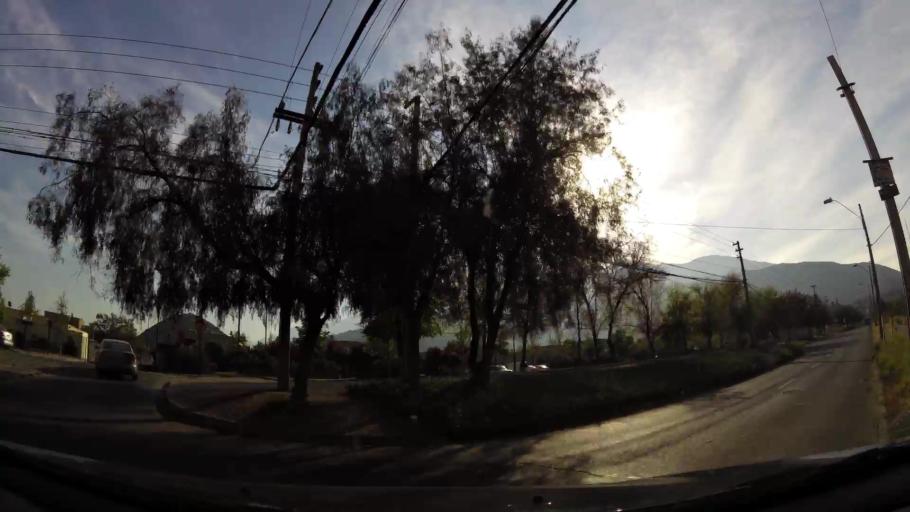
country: CL
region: Santiago Metropolitan
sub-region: Provincia de Cordillera
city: Puente Alto
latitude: -33.5599
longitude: -70.5493
